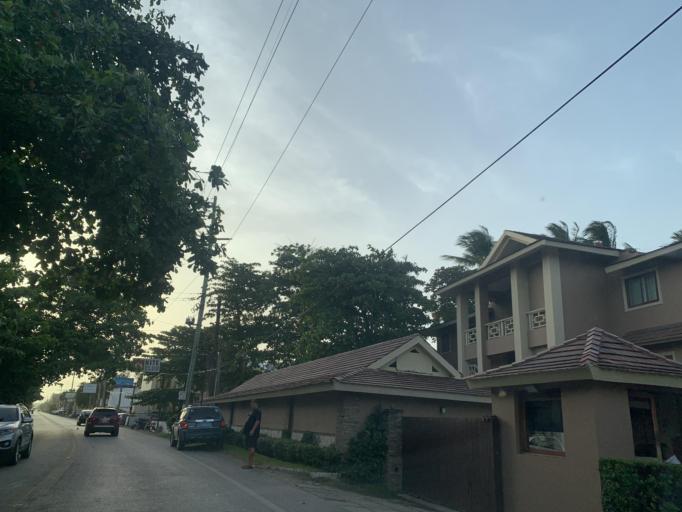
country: DO
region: Puerto Plata
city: Cabarete
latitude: 19.7621
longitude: -70.4217
